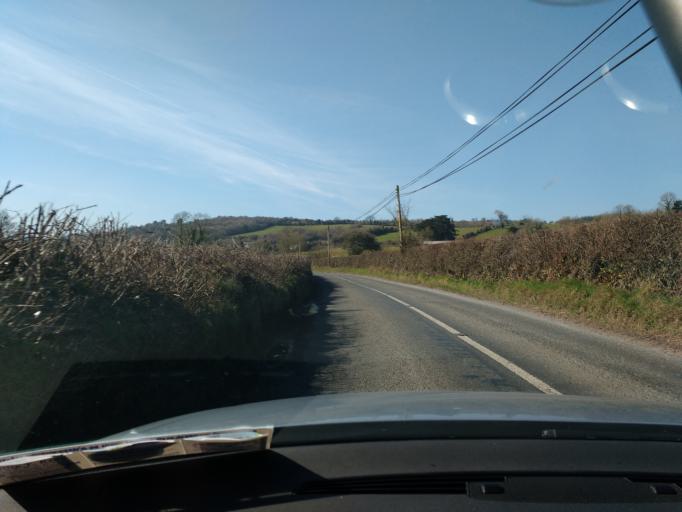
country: IE
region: Munster
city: Thurles
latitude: 52.6901
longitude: -7.9341
